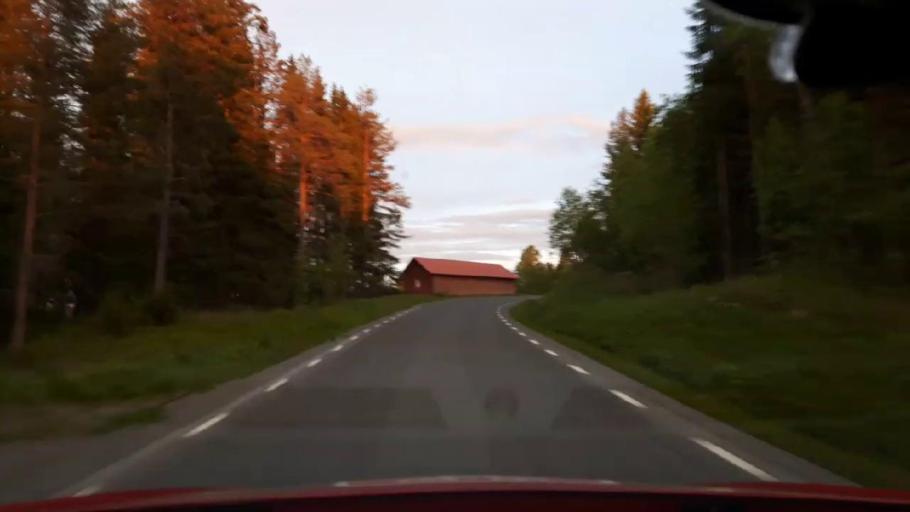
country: SE
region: Jaemtland
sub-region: OEstersunds Kommun
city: Brunflo
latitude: 63.0604
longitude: 14.8060
